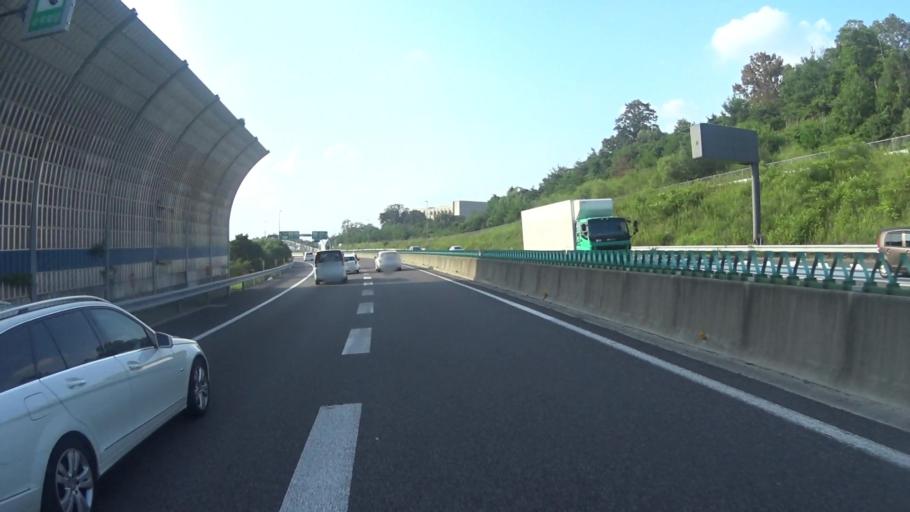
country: JP
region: Shiga Prefecture
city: Kusatsu
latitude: 34.9779
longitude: 135.9618
